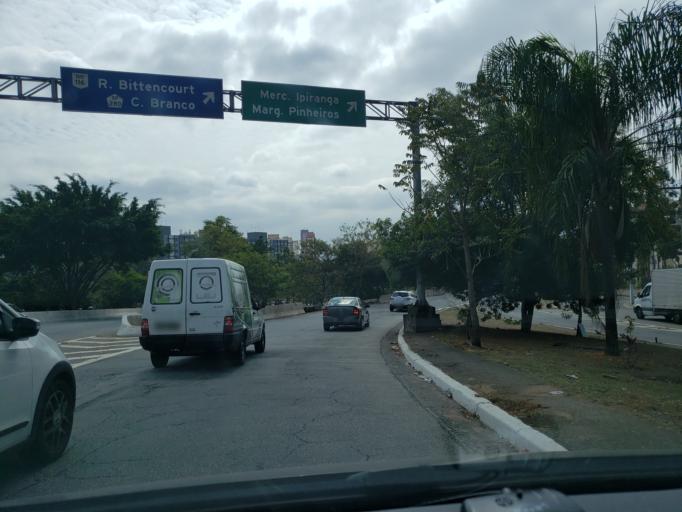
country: BR
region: Sao Paulo
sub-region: Sao Caetano Do Sul
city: Sao Caetano do Sul
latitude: -23.6043
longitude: -46.5998
